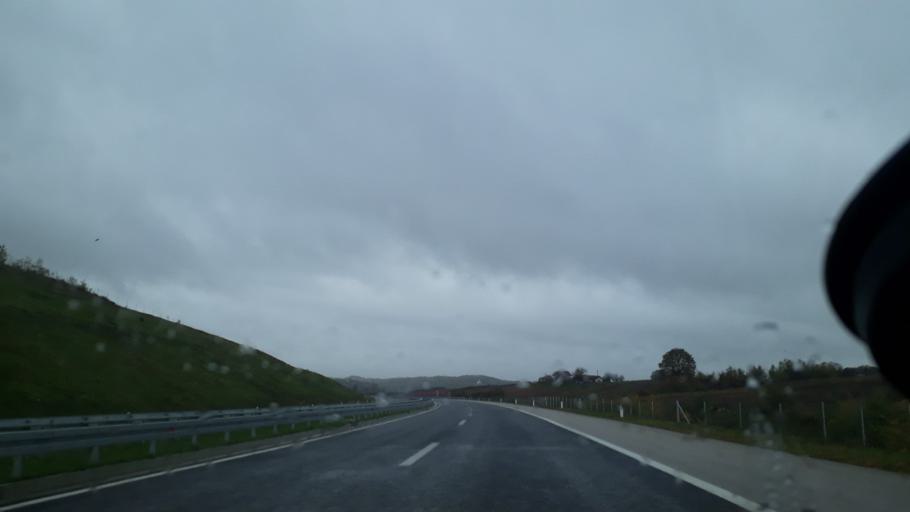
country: BA
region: Republika Srpska
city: Stanari
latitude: 44.8346
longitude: 17.9356
